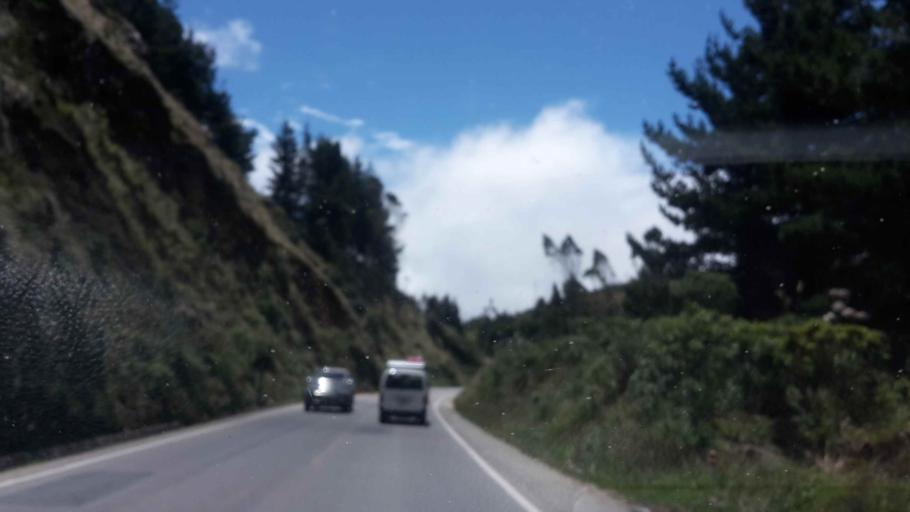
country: BO
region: Cochabamba
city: Colomi
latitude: -17.2716
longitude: -65.8775
